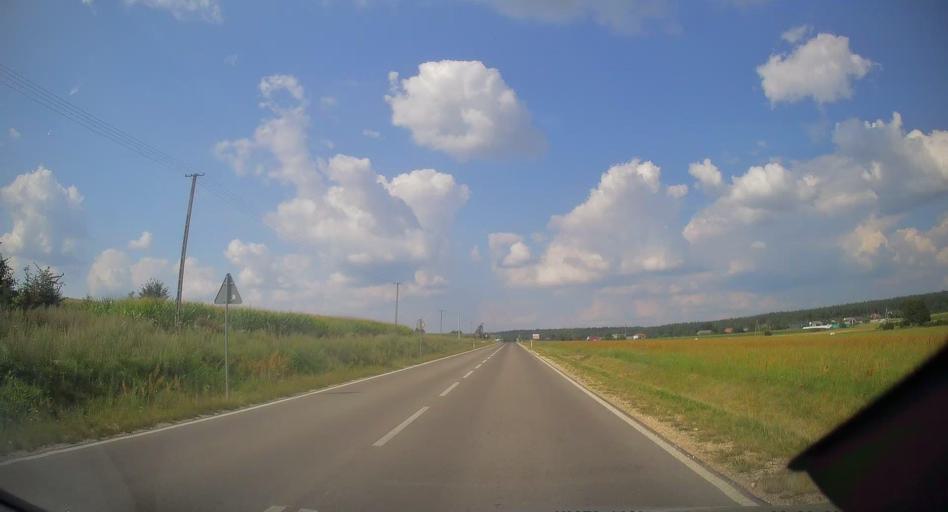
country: PL
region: Swietokrzyskie
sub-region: Powiat kielecki
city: Lopuszno
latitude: 50.9944
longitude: 20.2673
